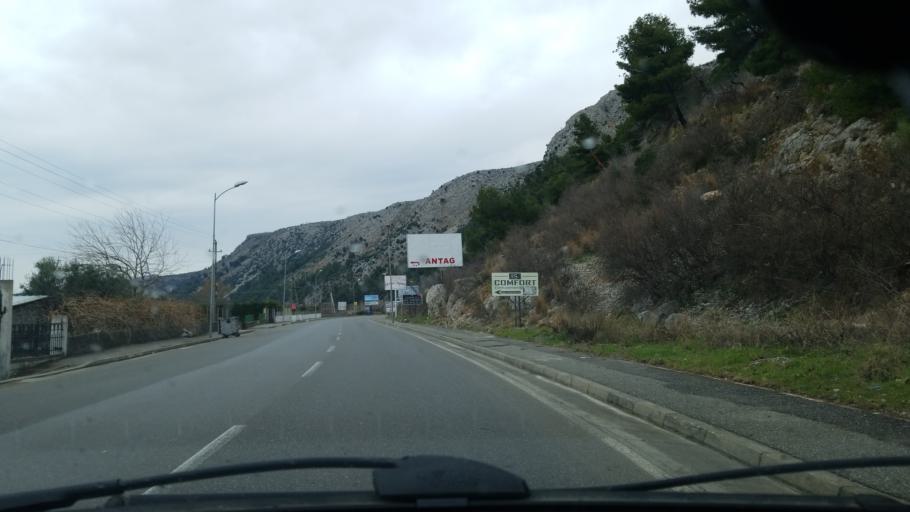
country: AL
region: Lezhe
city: Shengjin
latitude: 41.7996
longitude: 19.6174
